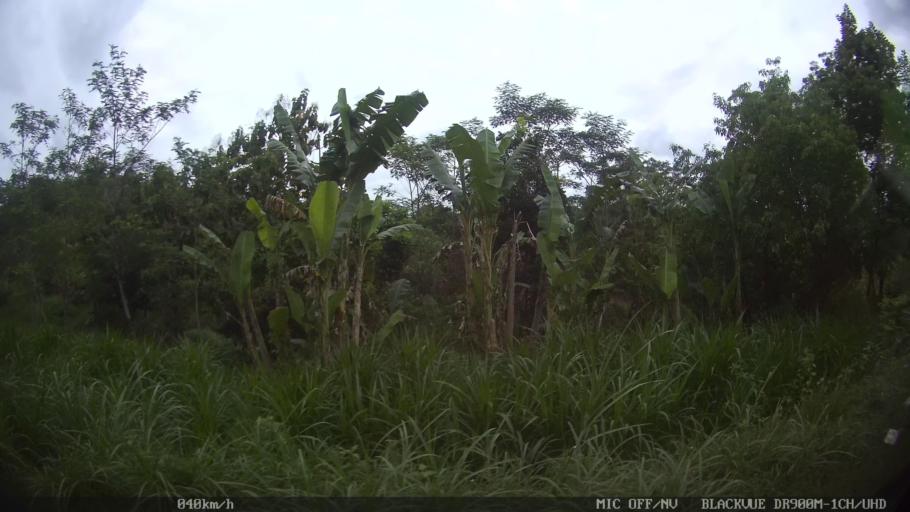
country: ID
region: Daerah Istimewa Yogyakarta
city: Sewon
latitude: -7.8614
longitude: 110.4216
